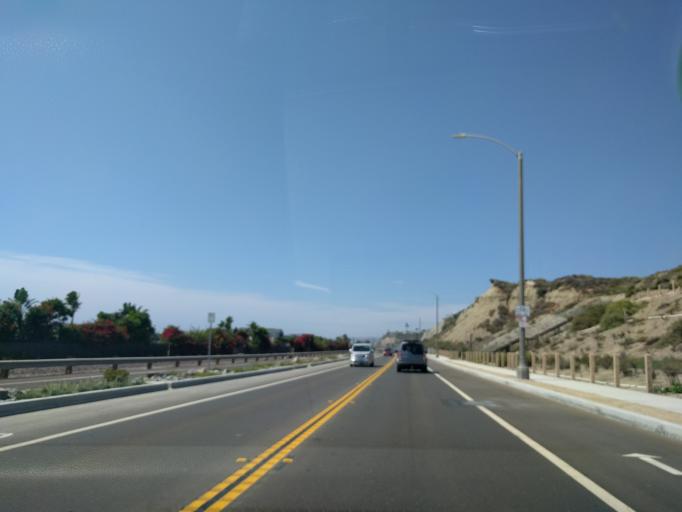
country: US
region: California
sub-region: Orange County
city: San Clemente
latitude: 33.4361
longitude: -117.6377
